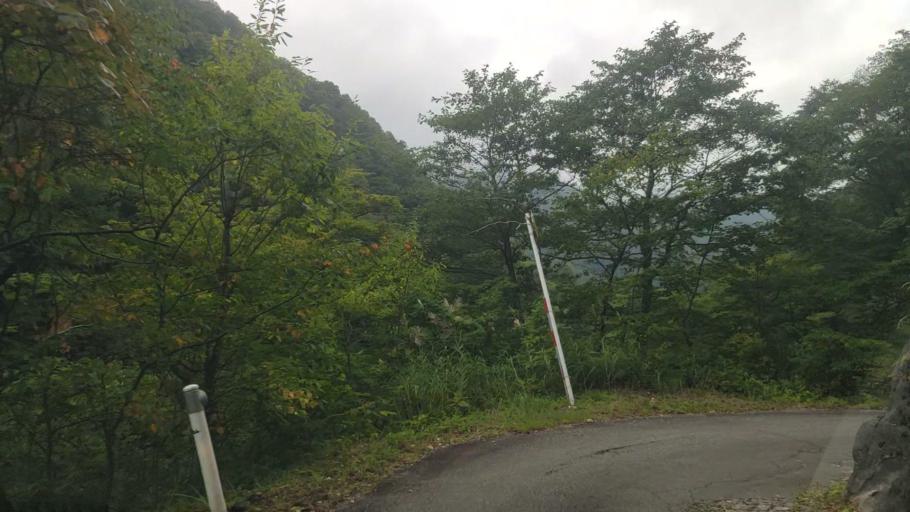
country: JP
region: Toyama
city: Yatsuomachi-higashikumisaka
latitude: 36.3942
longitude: 137.0782
